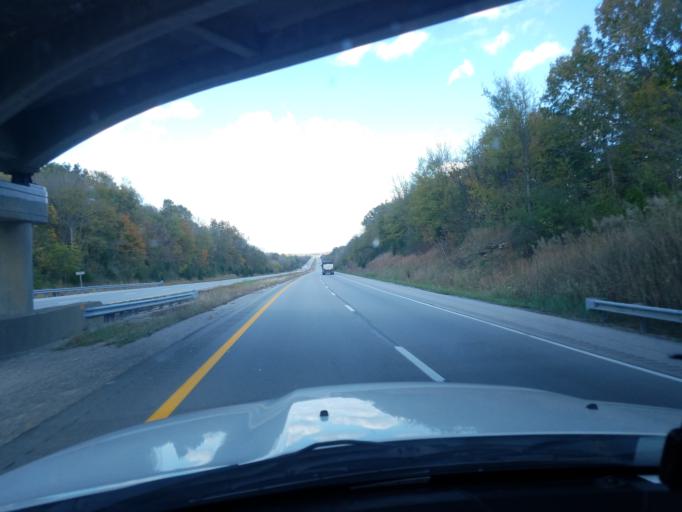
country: US
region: Kentucky
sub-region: Butler County
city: Morgantown
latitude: 37.2672
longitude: -86.7481
